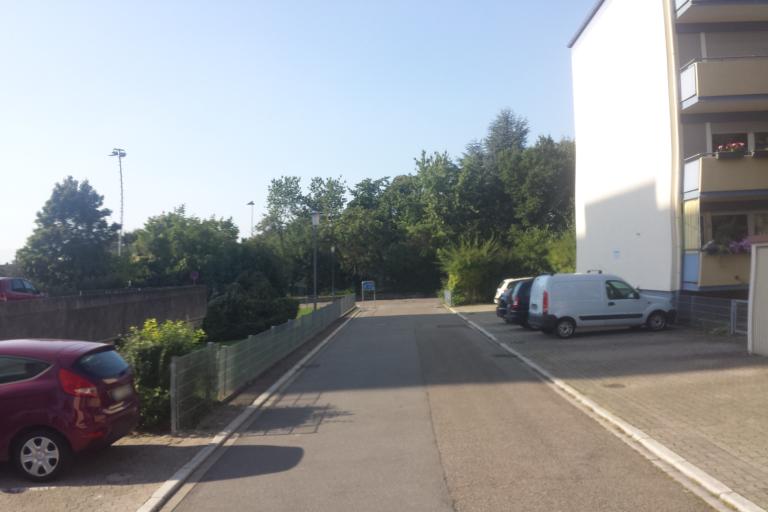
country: DE
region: Baden-Wuerttemberg
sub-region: Karlsruhe Region
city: Eppelheim
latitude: 49.4061
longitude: 8.6269
